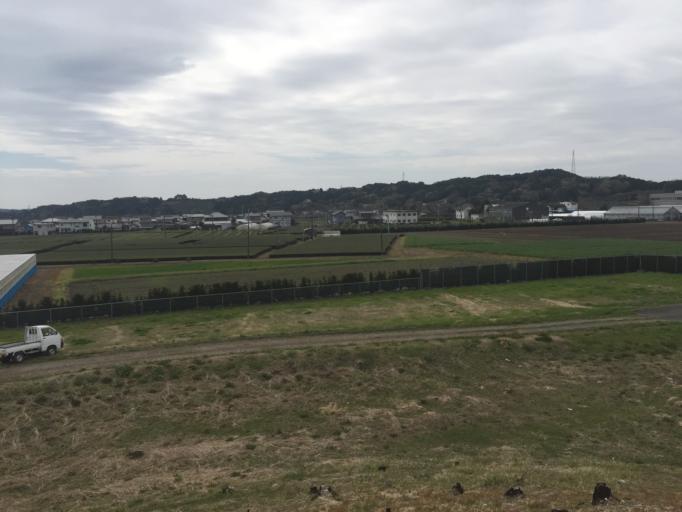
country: JP
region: Shizuoka
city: Mori
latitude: 34.7976
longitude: 137.9469
